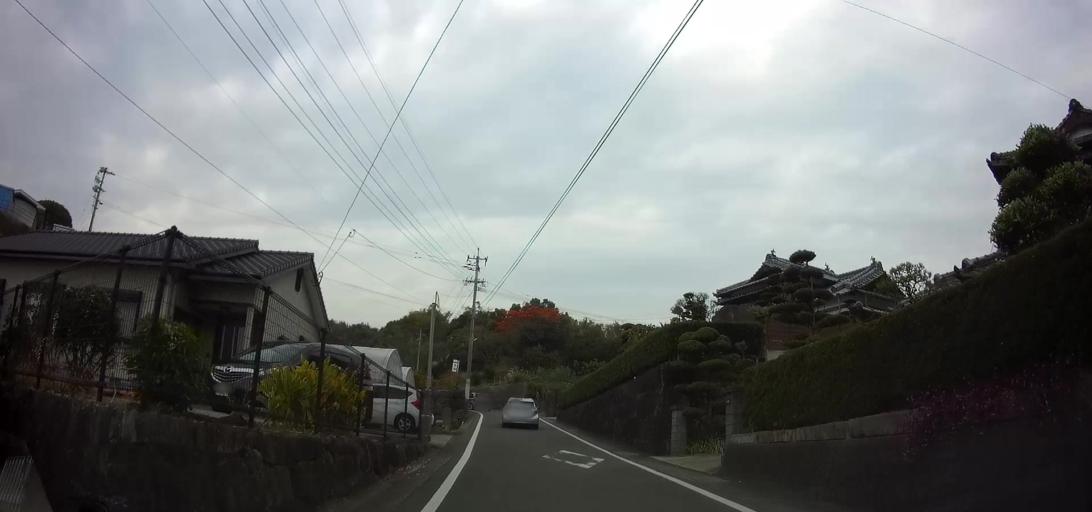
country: JP
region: Nagasaki
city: Shimabara
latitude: 32.6364
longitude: 130.2449
